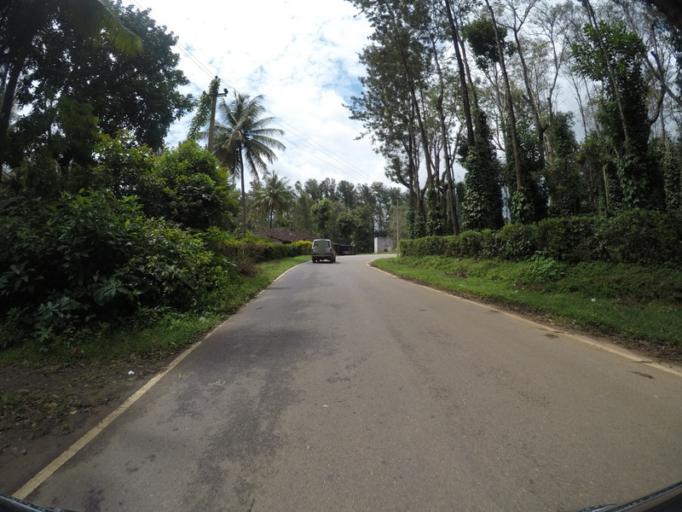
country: IN
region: Karnataka
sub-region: Kodagu
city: Suntikoppa
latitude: 12.4683
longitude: 75.8299
